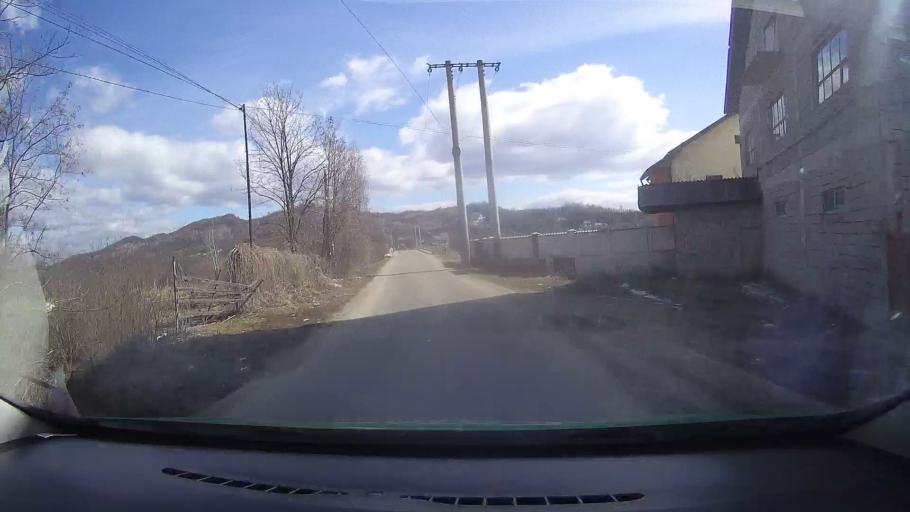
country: RO
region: Dambovita
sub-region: Comuna Branesti
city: Branesti
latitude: 45.0311
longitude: 25.4177
